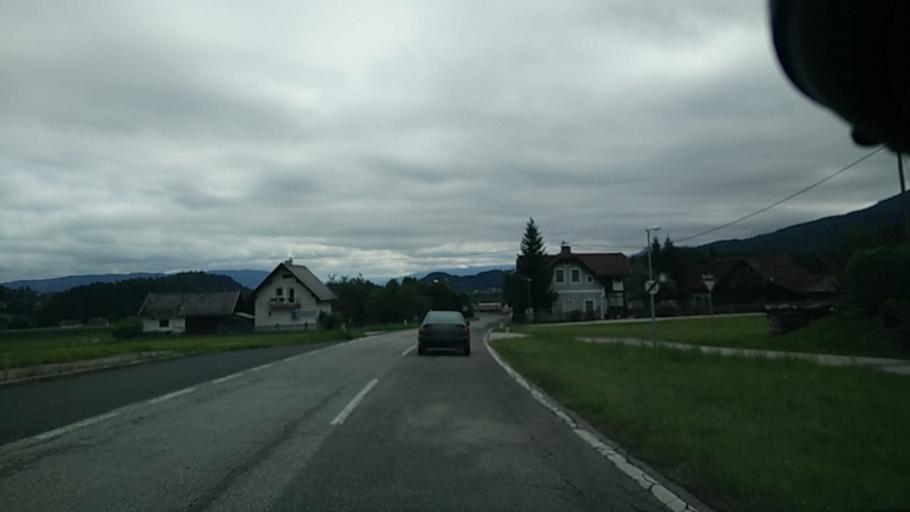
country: AT
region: Carinthia
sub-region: Politischer Bezirk Villach Land
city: Rosegg
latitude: 46.5547
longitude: 13.9782
